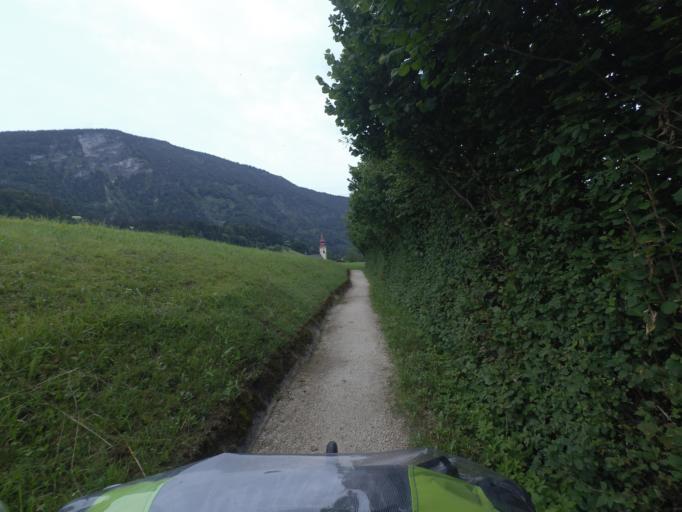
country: AT
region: Salzburg
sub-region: Politischer Bezirk Zell am See
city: Unken
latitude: 47.6473
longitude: 12.7265
